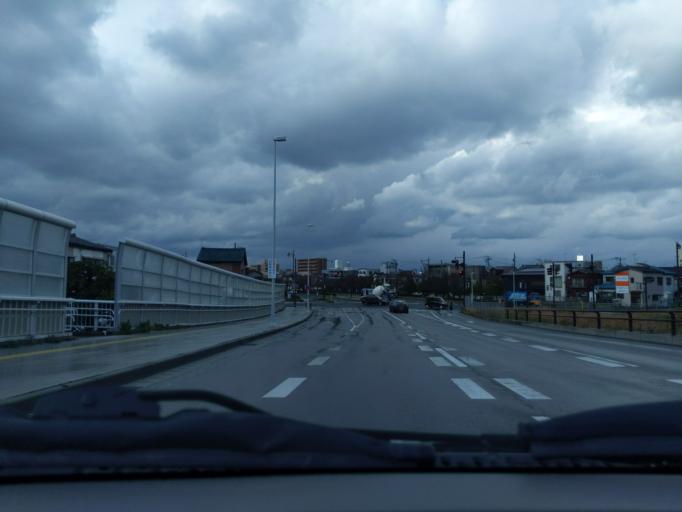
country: JP
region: Niigata
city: Niigata-shi
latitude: 37.9245
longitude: 139.0534
